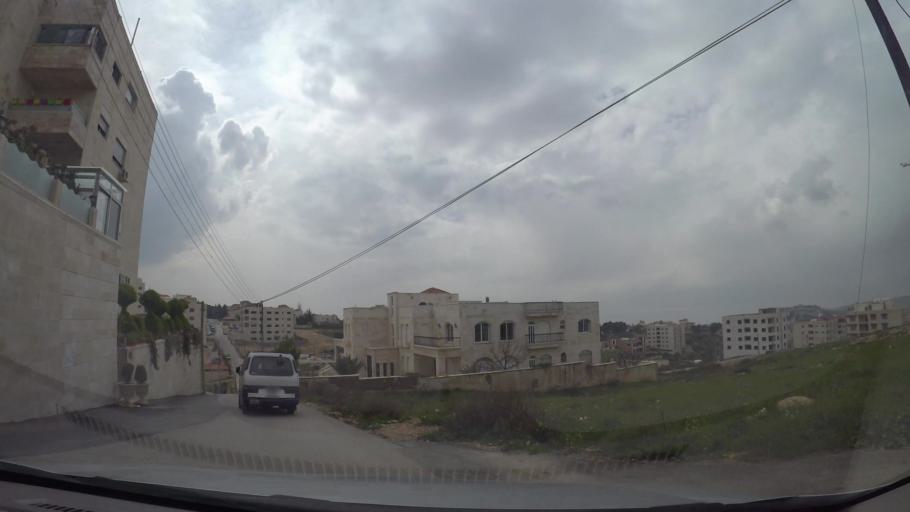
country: JO
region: Amman
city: Umm as Summaq
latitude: 31.9009
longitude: 35.8312
